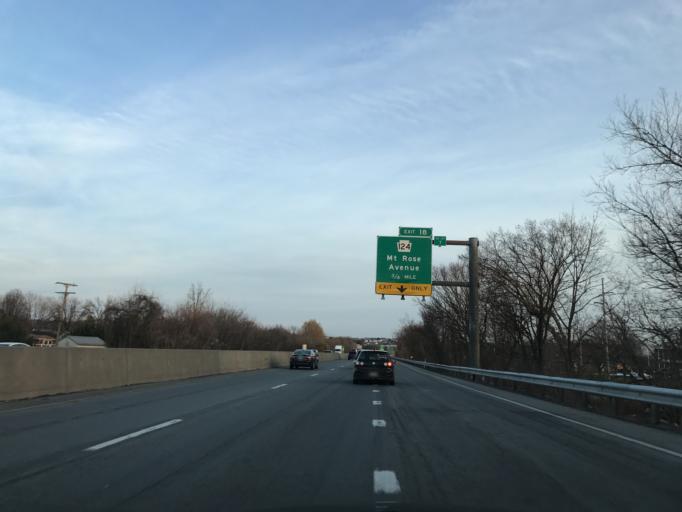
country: US
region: Pennsylvania
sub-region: York County
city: East York
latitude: 39.9699
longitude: -76.6922
